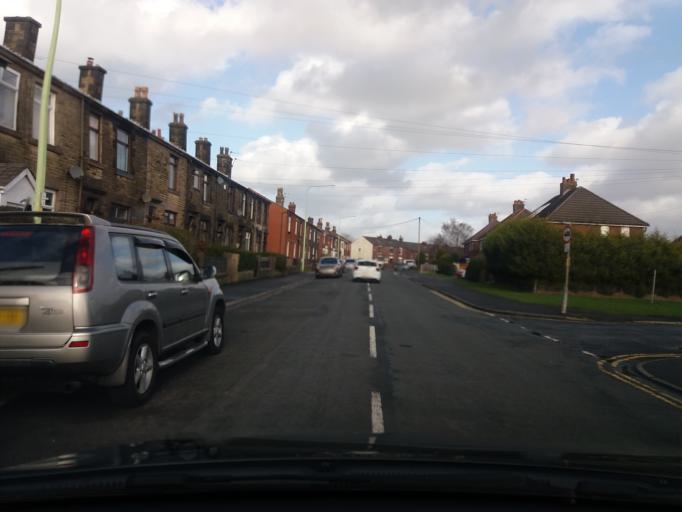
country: GB
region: England
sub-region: Lancashire
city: Adlington
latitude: 53.6107
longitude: -2.6139
